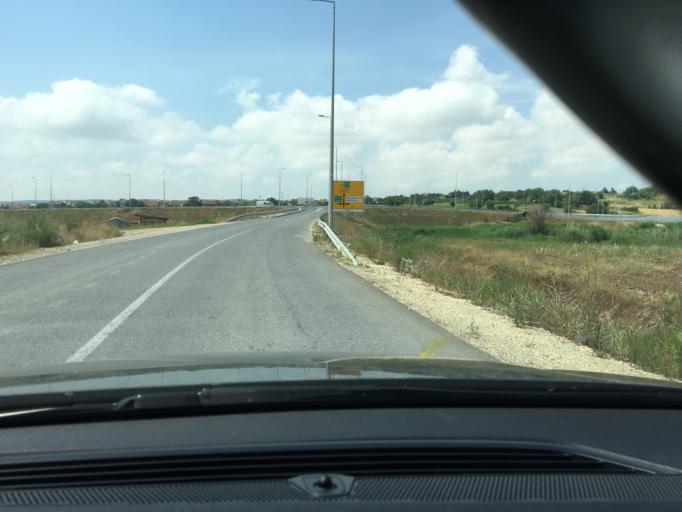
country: MK
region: Sveti Nikole
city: Sveti Nikole
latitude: 41.8793
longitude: 21.9395
